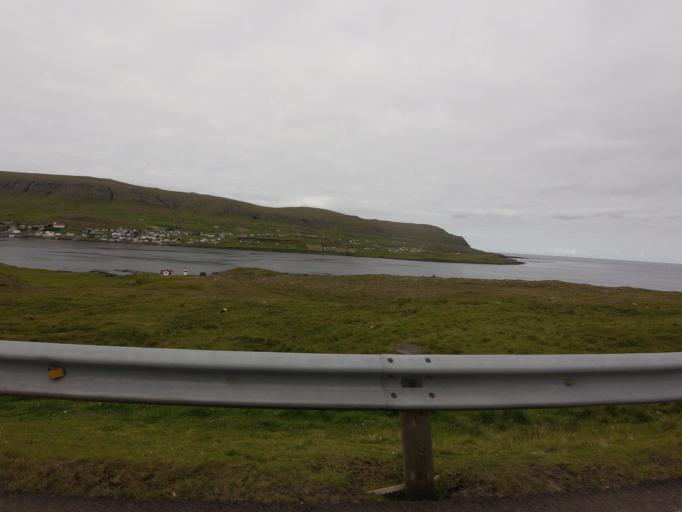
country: FO
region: Suduroy
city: Tvoroyri
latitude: 61.5411
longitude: -6.8045
